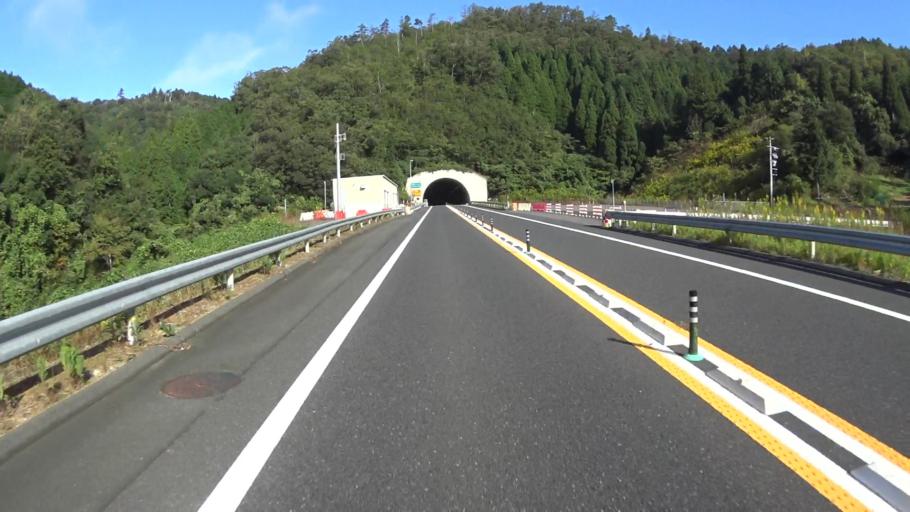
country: JP
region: Kyoto
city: Ayabe
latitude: 35.3205
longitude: 135.3172
